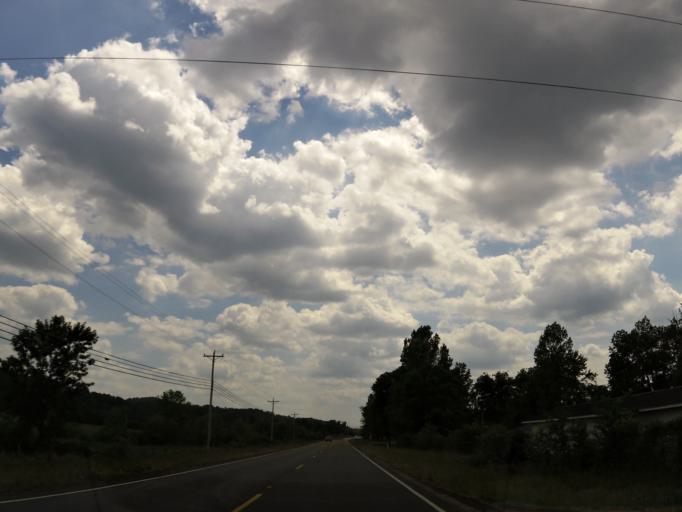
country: US
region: Tennessee
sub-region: Bledsoe County
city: Pikeville
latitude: 35.5144
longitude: -85.2810
